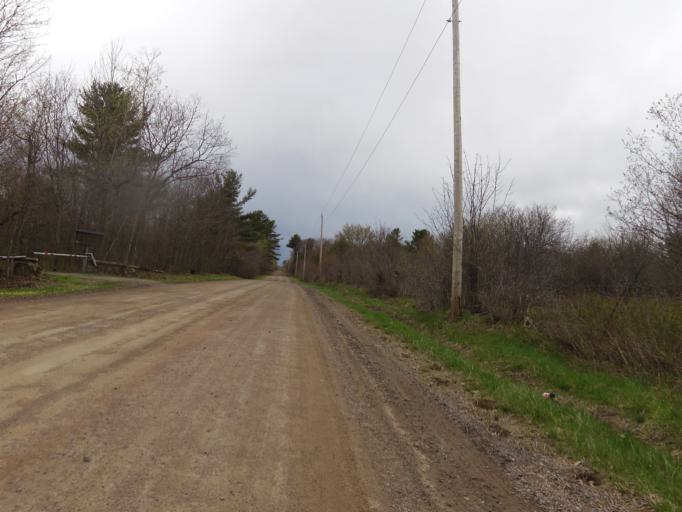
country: CA
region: Quebec
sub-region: Laurentides
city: Brownsburg-Chatham
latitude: 45.6136
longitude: -74.4910
